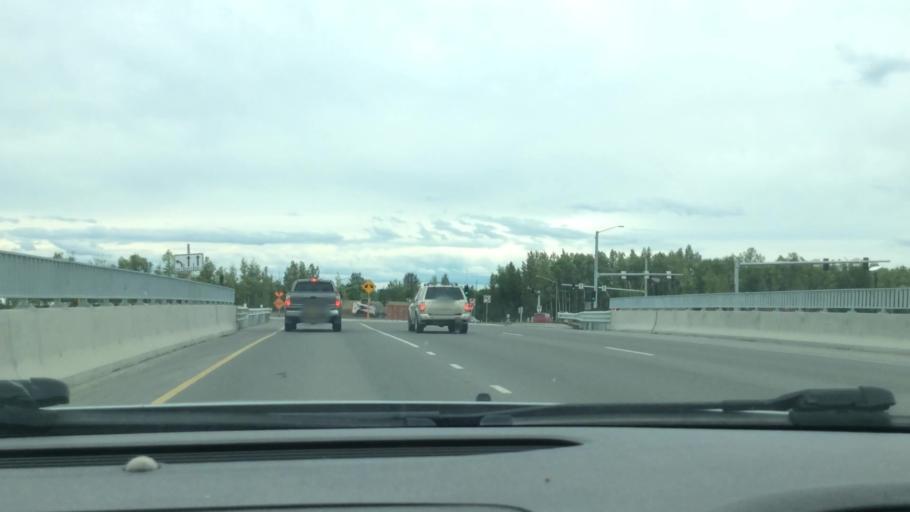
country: US
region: Alaska
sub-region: Anchorage Municipality
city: Elmendorf Air Force Base
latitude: 61.2271
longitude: -149.7341
